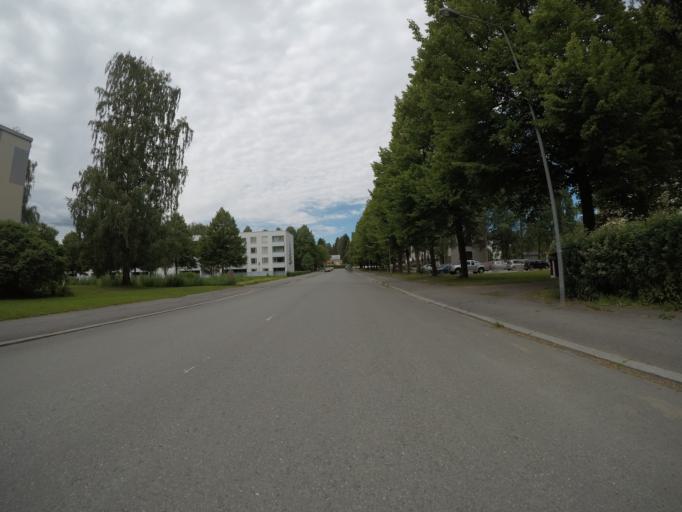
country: FI
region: Haeme
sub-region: Haemeenlinna
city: Haemeenlinna
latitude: 61.0063
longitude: 24.4445
